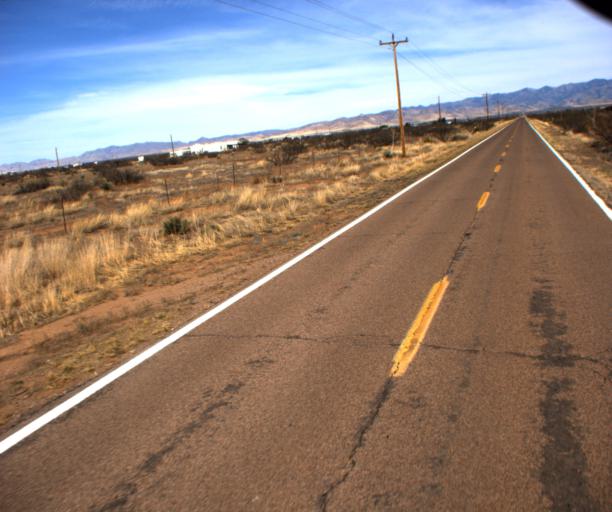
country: US
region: Arizona
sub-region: Cochise County
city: Willcox
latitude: 31.8762
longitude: -109.6188
